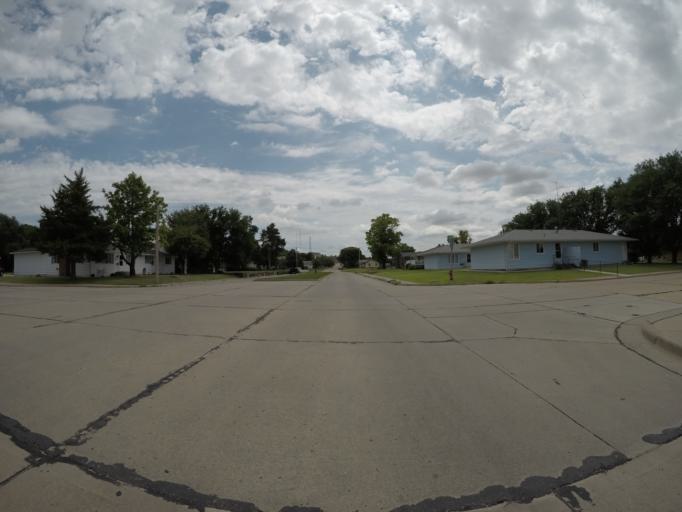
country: US
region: Kansas
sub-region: Rawlins County
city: Atwood
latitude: 39.8047
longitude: -101.0422
